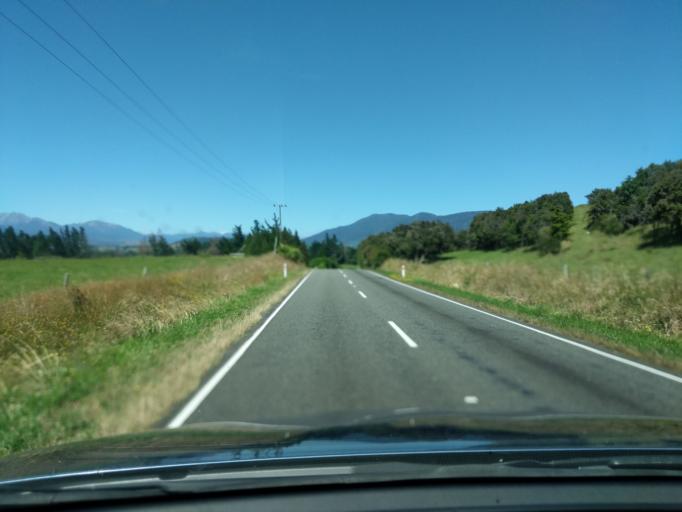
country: NZ
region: Tasman
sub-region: Tasman District
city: Takaka
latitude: -40.6924
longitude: 172.6421
